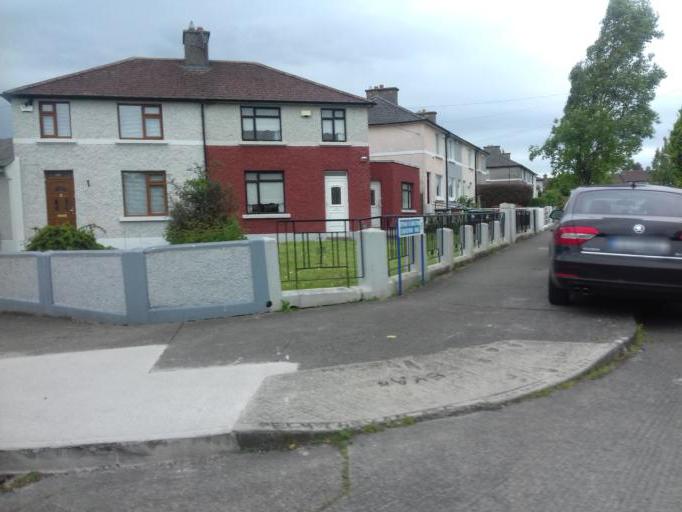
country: IE
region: Leinster
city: Drumcondra
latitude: 53.3713
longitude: -6.2593
